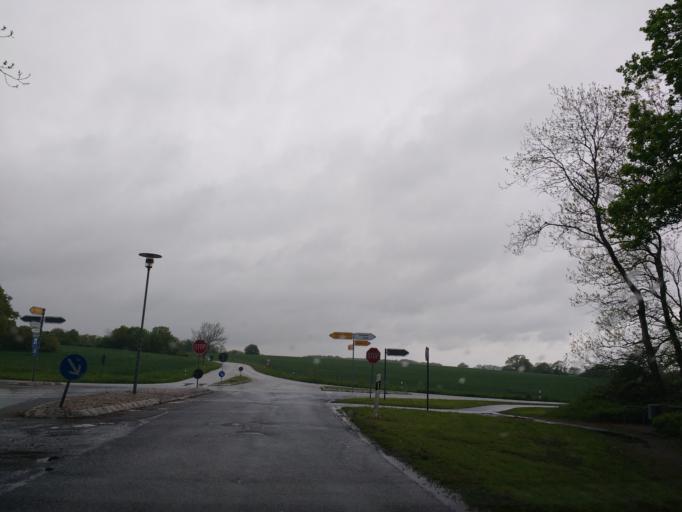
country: DE
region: Schleswig-Holstein
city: Damp
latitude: 54.5733
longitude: 9.9598
